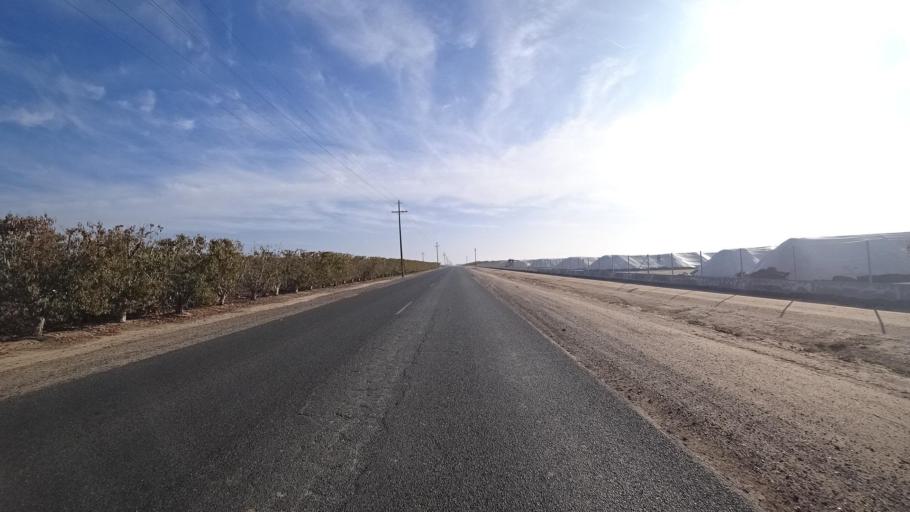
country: US
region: California
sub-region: Kern County
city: McFarland
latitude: 35.6021
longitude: -119.1895
